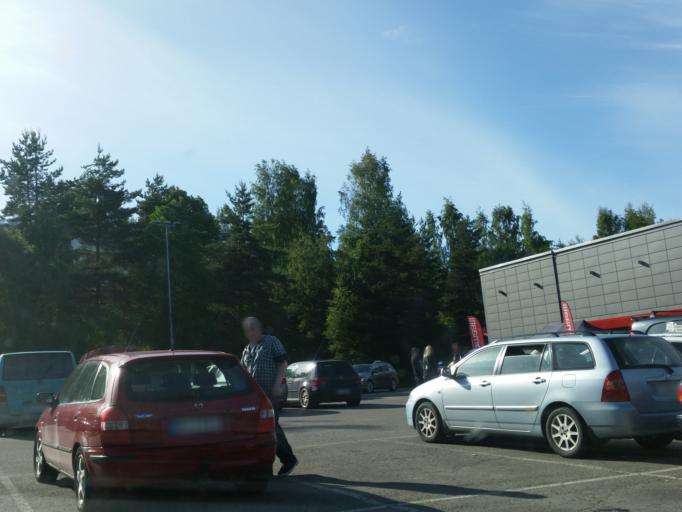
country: FI
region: Northern Savo
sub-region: Kuopio
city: Kuopio
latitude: 62.9064
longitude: 27.6835
